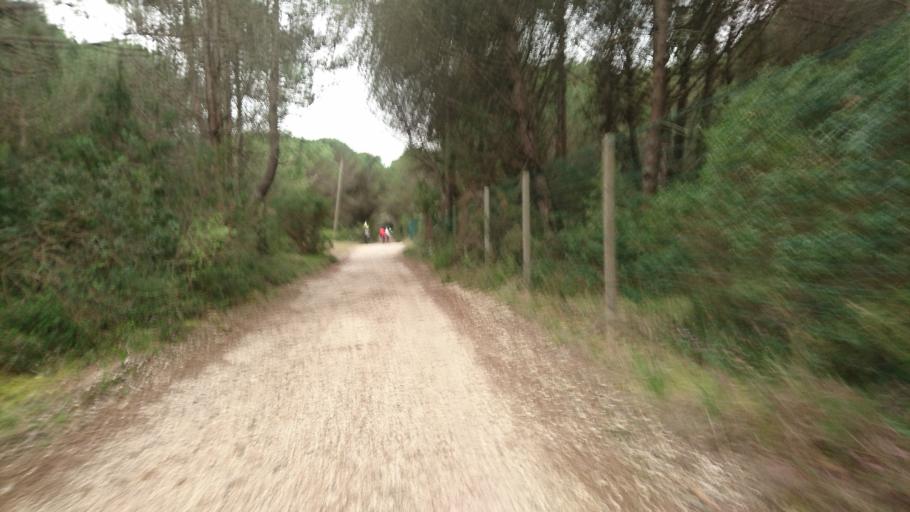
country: IT
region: Friuli Venezia Giulia
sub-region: Provincia di Udine
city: Lignano Sabbiadoro
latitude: 45.6428
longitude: 13.0947
